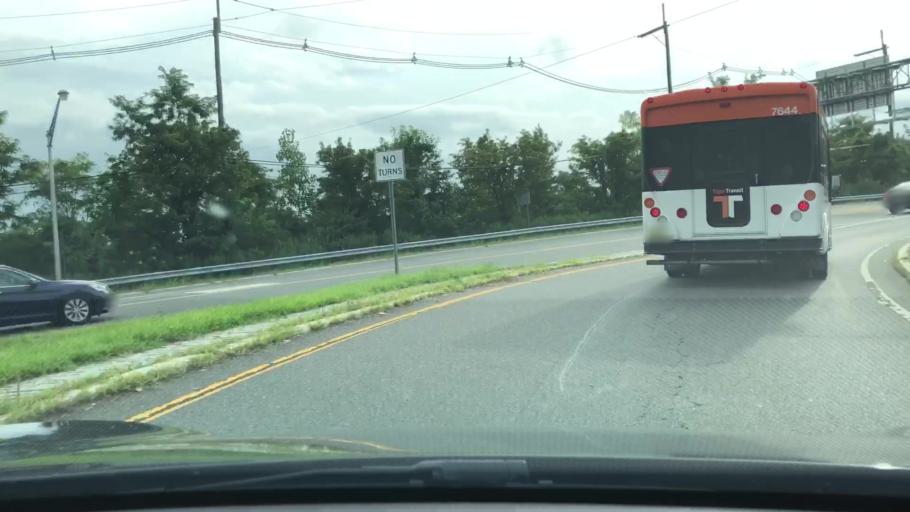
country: US
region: New Jersey
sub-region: Mercer County
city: Princeton
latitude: 40.3114
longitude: -74.6598
